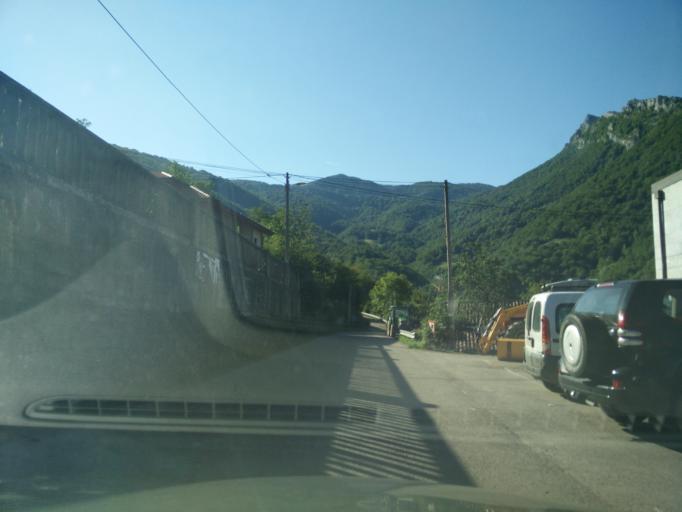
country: ES
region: Asturias
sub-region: Province of Asturias
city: Amieva
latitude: 43.1880
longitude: -5.1642
